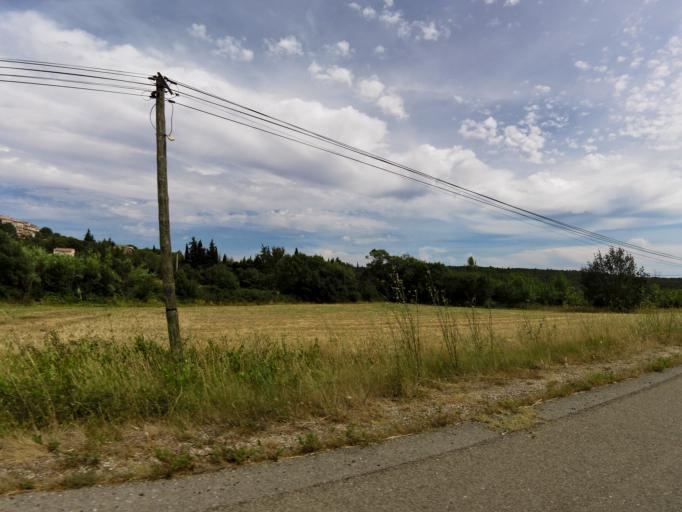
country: FR
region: Languedoc-Roussillon
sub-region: Departement du Gard
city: Saint-Mamert-du-Gard
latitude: 43.8498
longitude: 4.1507
